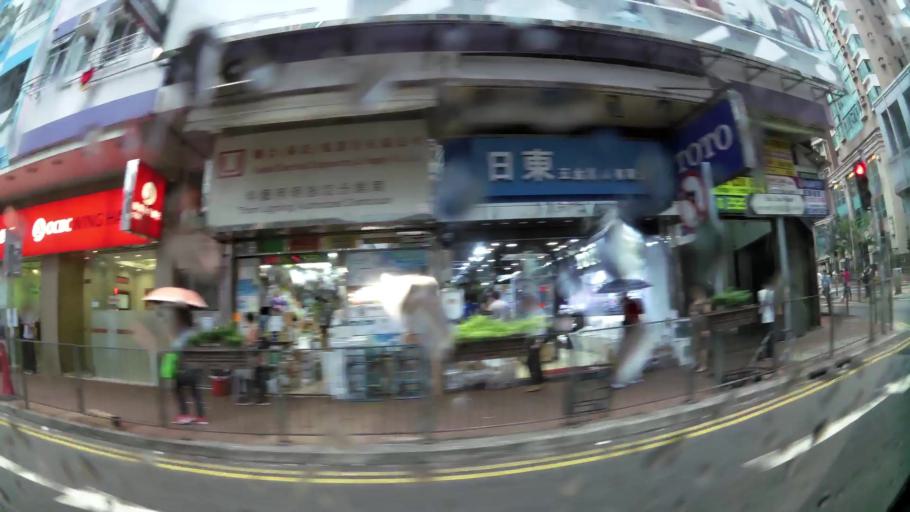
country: HK
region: Tsuen Wan
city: Tsuen Wan
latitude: 22.3684
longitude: 114.1190
